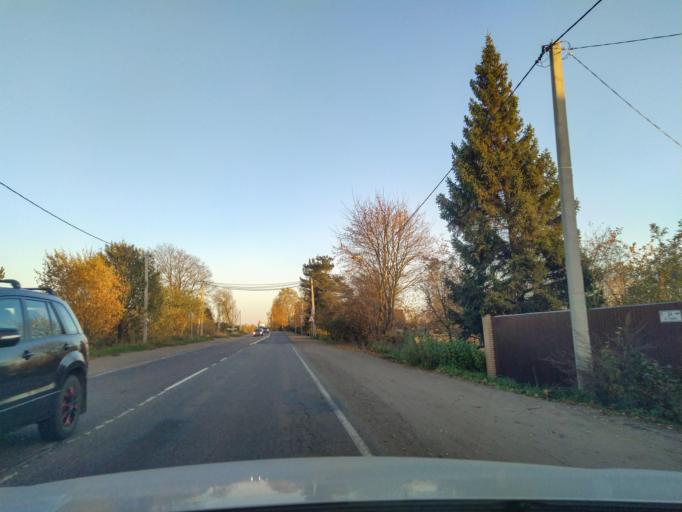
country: RU
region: Leningrad
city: Maloye Verevo
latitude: 59.6138
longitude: 30.2200
